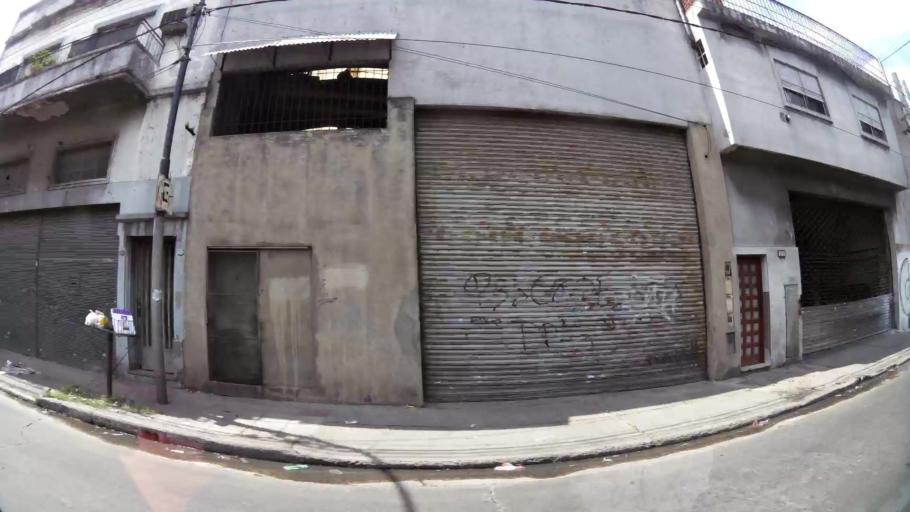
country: AR
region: Buenos Aires
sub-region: Partido de Lanus
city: Lanus
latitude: -34.6751
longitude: -58.4093
